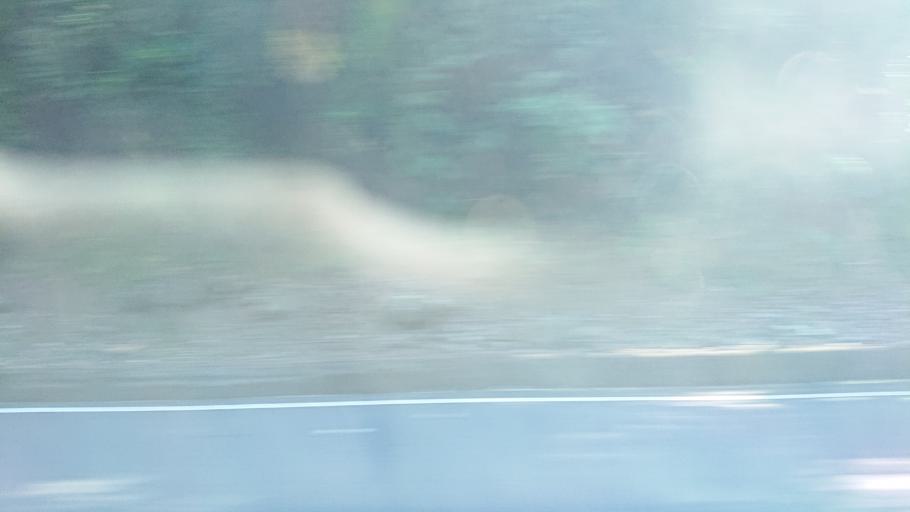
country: TW
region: Taiwan
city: Lugu
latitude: 23.4861
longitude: 120.7503
